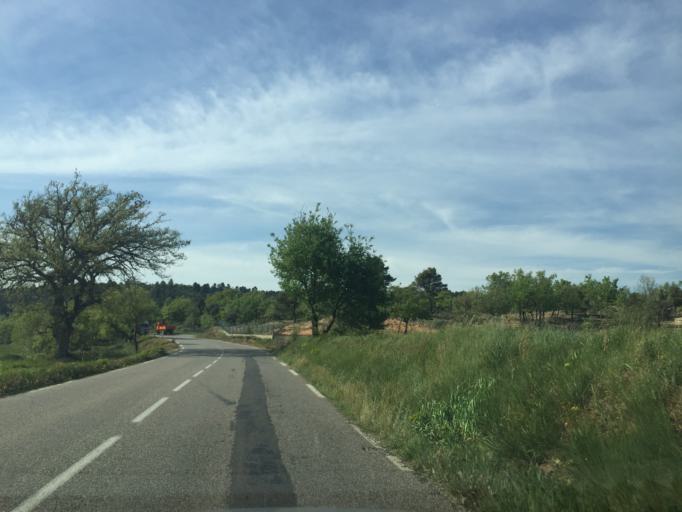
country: FR
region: Provence-Alpes-Cote d'Azur
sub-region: Departement du Var
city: Vinon-sur-Verdon
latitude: 43.7021
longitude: 5.8282
